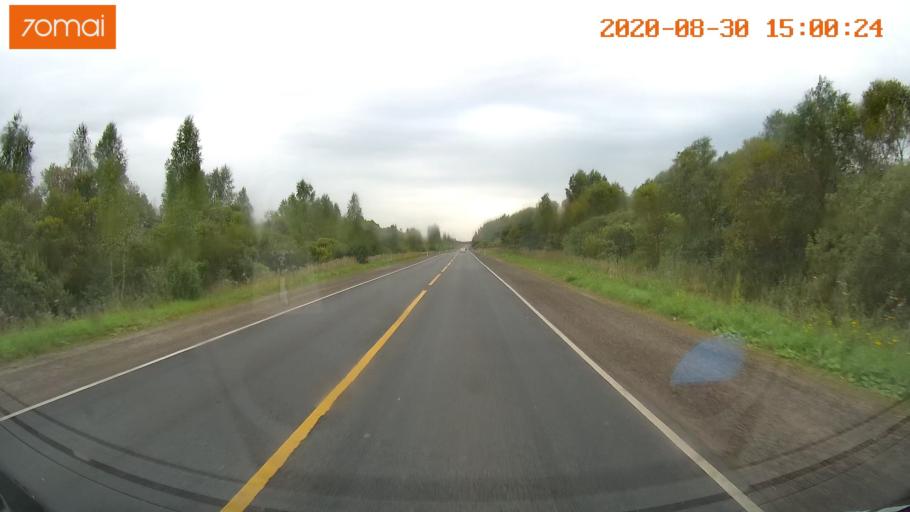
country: RU
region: Ivanovo
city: Staraya Vichuga
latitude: 57.3318
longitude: 41.9583
